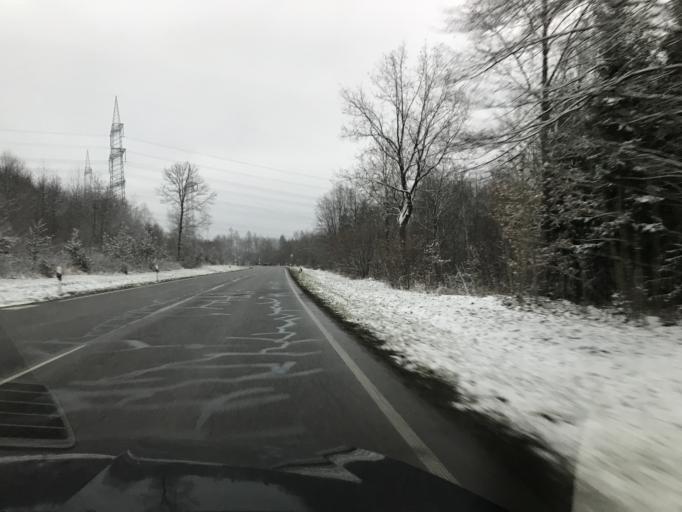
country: DE
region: Baden-Wuerttemberg
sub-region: Regierungsbezirk Stuttgart
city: Altbach
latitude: 48.7391
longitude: 9.3865
